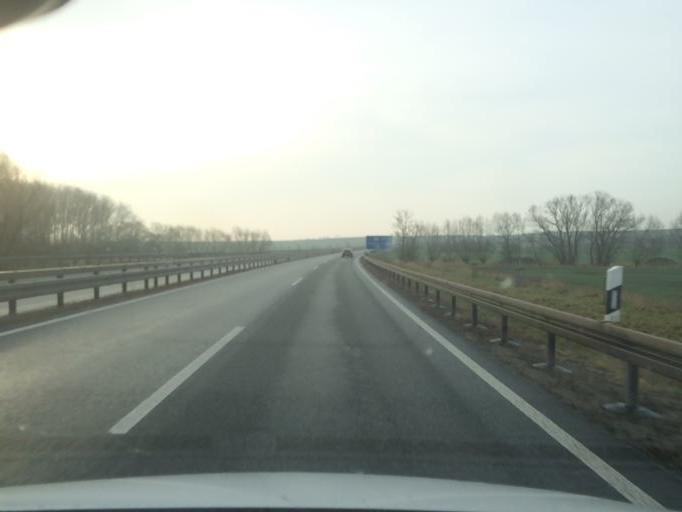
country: DE
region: Thuringia
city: Wipperdorf
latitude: 51.5005
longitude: 10.7084
